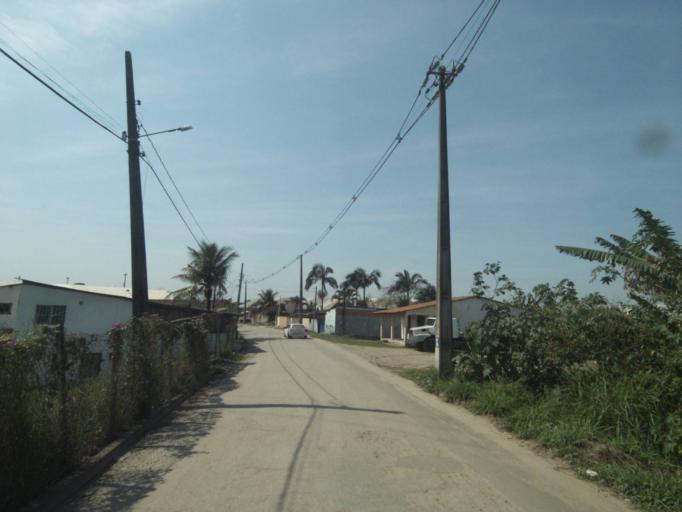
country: BR
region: Parana
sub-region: Paranagua
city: Paranagua
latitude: -25.5510
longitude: -48.5590
